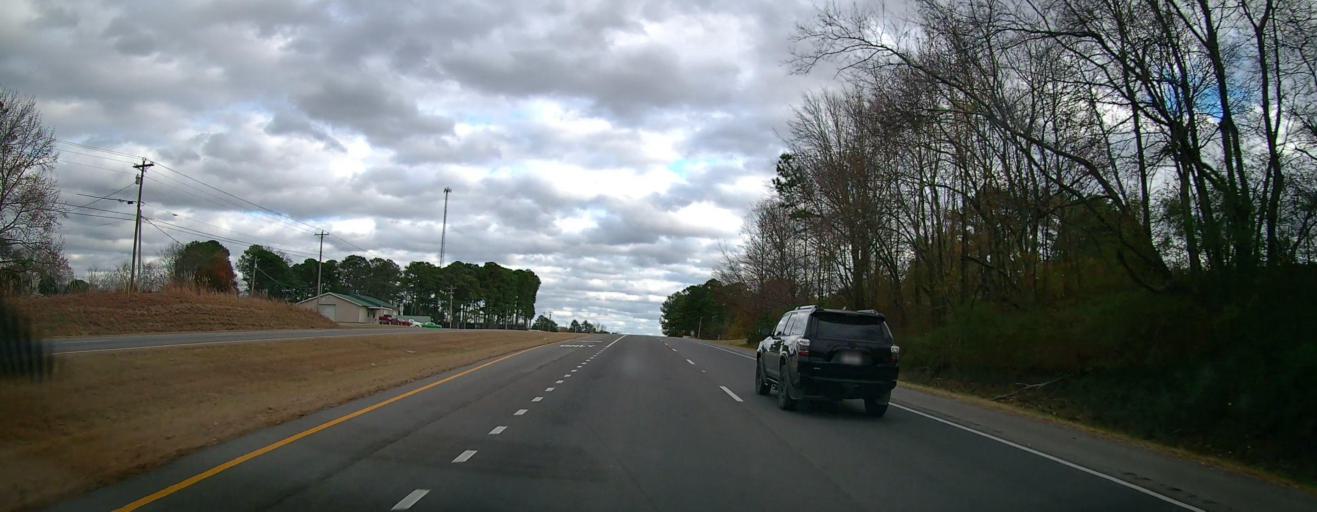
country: US
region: Alabama
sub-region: Cullman County
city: Cullman
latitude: 34.2298
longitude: -86.9114
